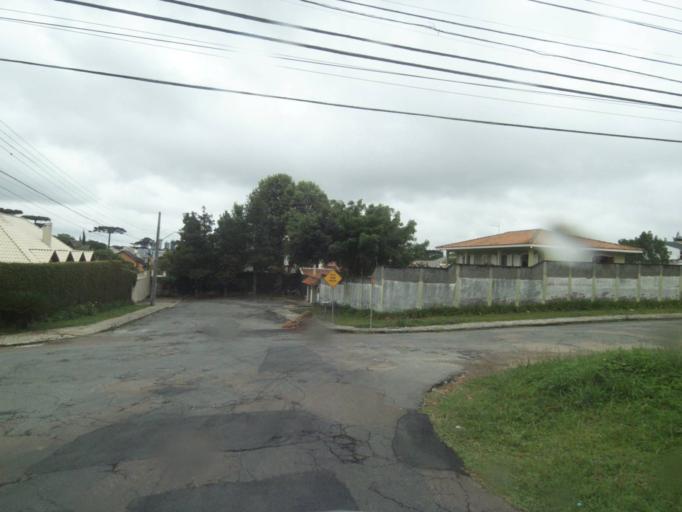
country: BR
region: Parana
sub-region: Curitiba
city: Curitiba
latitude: -25.4242
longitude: -49.3231
